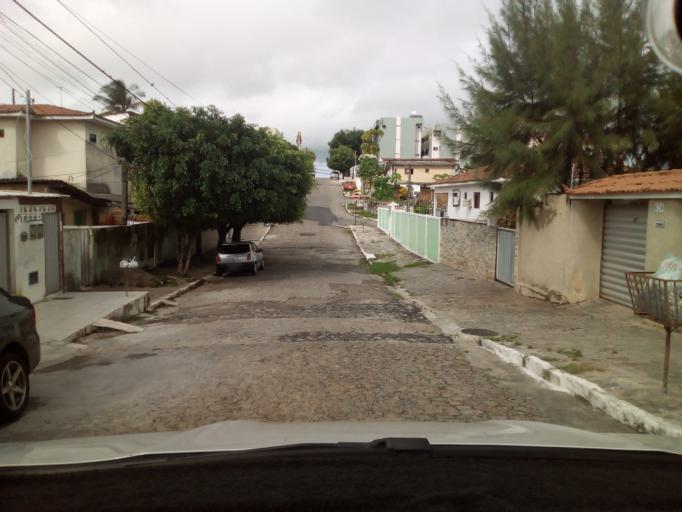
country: BR
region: Paraiba
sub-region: Joao Pessoa
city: Joao Pessoa
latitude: -7.1253
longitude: -34.8529
